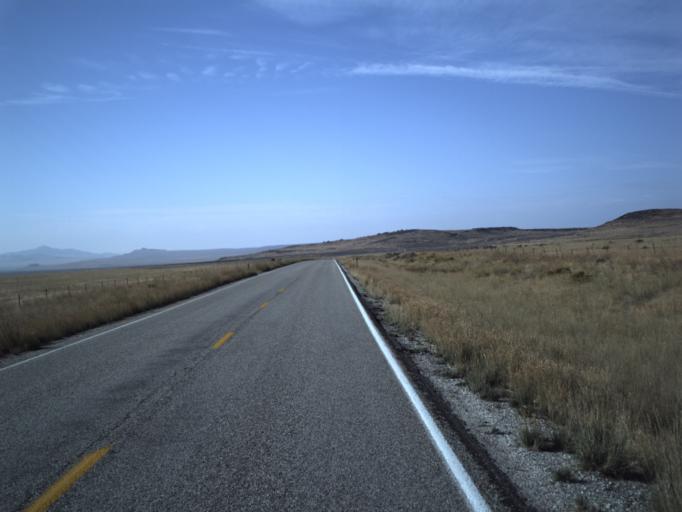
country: US
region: Idaho
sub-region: Minidoka County
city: Rupert
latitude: 41.8570
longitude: -113.1308
